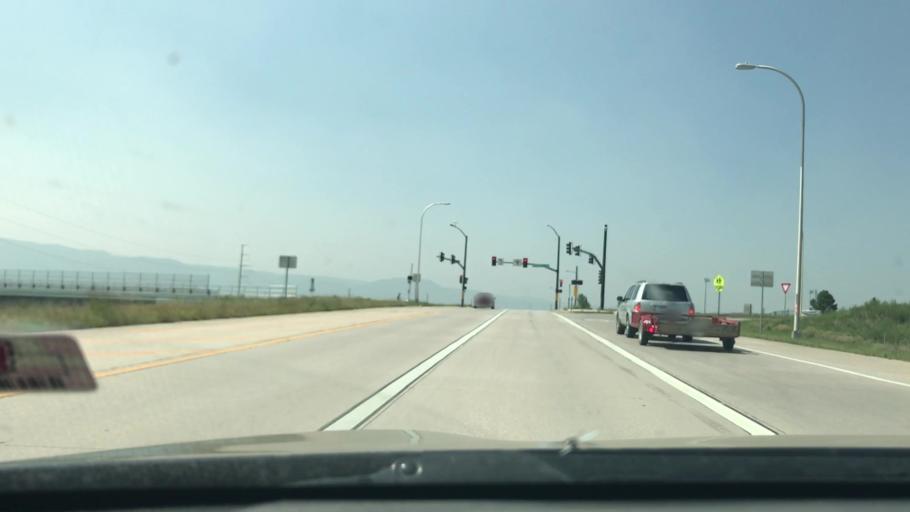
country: US
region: Colorado
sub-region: El Paso County
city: Black Forest
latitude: 38.9844
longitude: -104.7631
